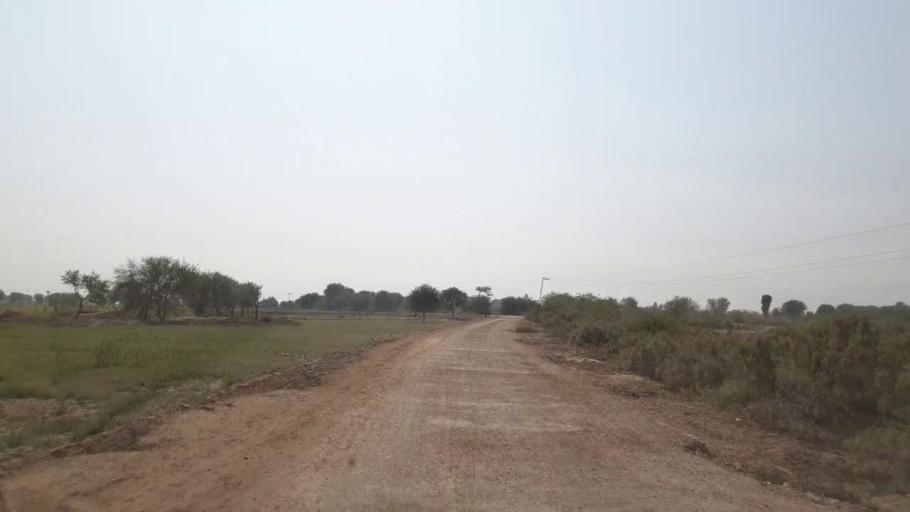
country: PK
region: Sindh
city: Mirpur Khas
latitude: 25.6319
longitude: 69.1433
